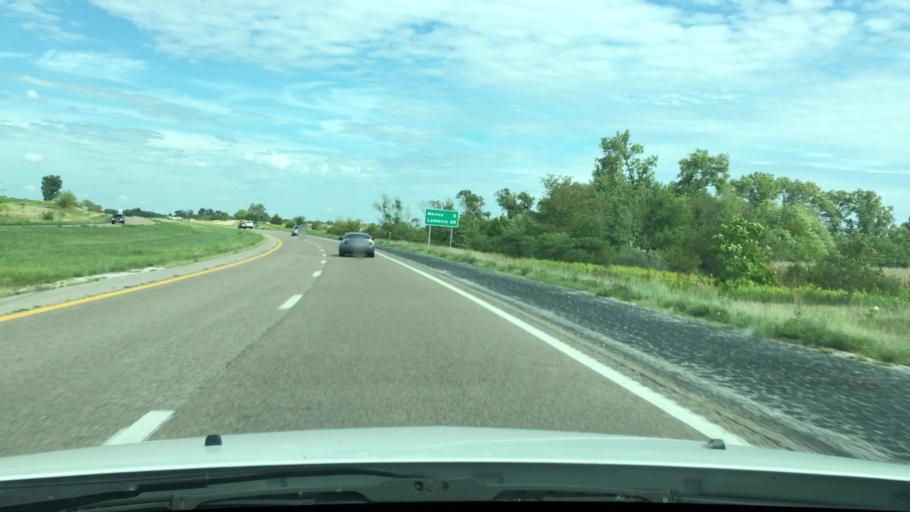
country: US
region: Missouri
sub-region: Audrain County
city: Mexico
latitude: 39.0291
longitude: -91.8857
